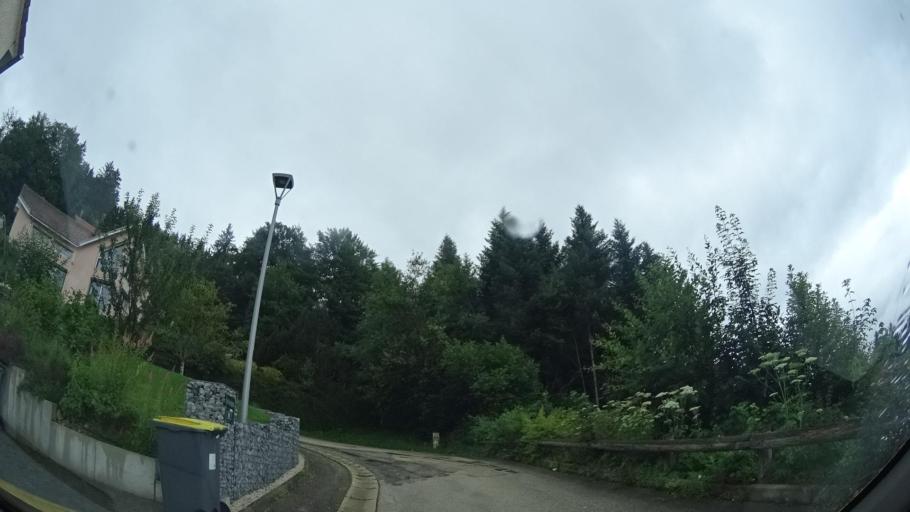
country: FR
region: Franche-Comte
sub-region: Departement du Doubs
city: Les Fourgs
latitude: 46.8321
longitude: 6.3454
